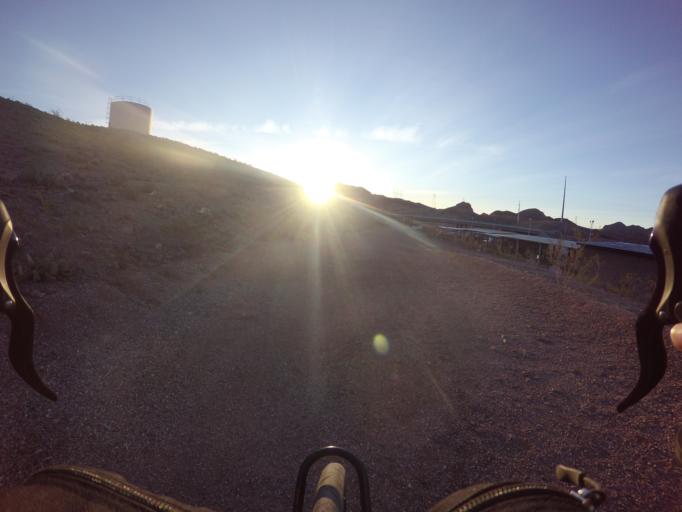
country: US
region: Nevada
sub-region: Clark County
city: Boulder City
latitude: 36.0163
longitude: -114.7578
